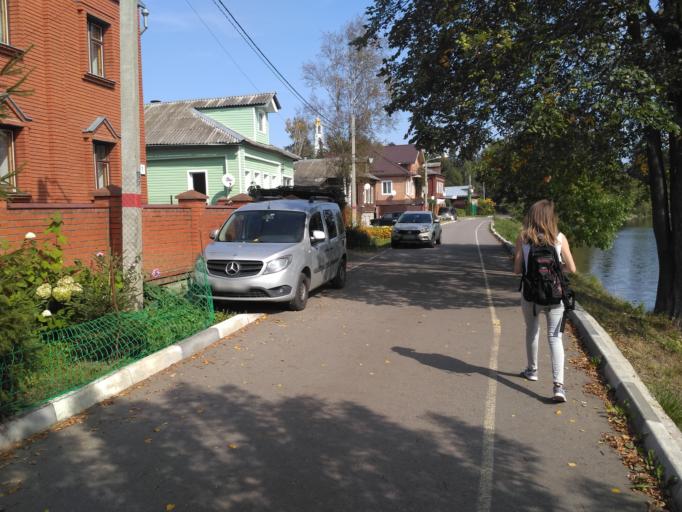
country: RU
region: Moskovskaya
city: Sergiyev Posad
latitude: 56.3051
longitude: 38.1263
